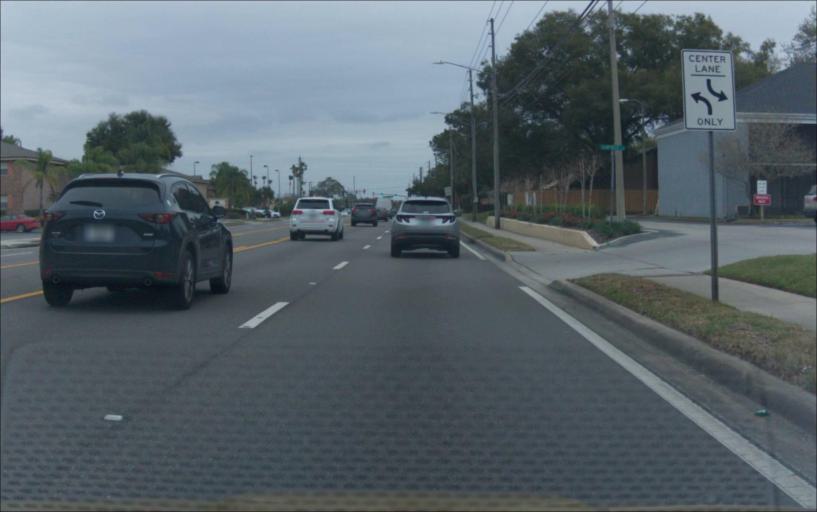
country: US
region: Florida
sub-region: Seminole County
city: Goldenrod
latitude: 28.6219
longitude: -81.3003
